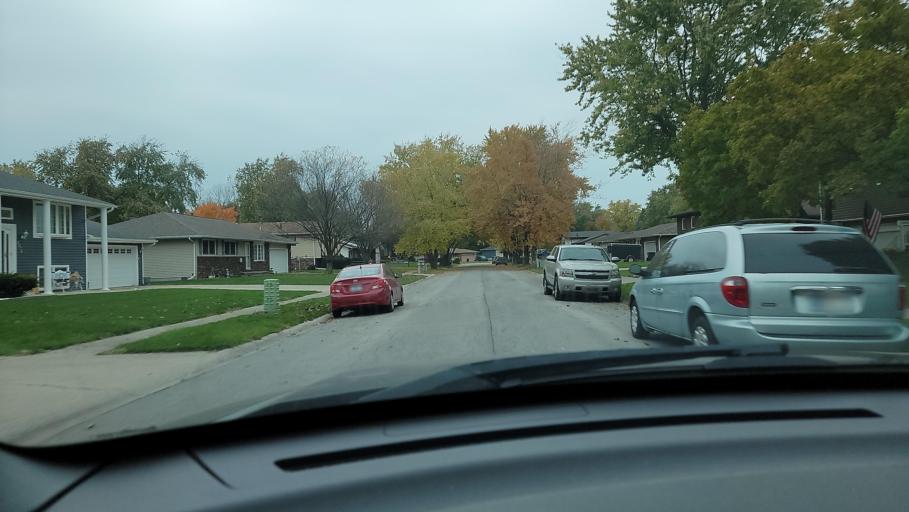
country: US
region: Indiana
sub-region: Porter County
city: Portage
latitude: 41.5623
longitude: -87.1808
